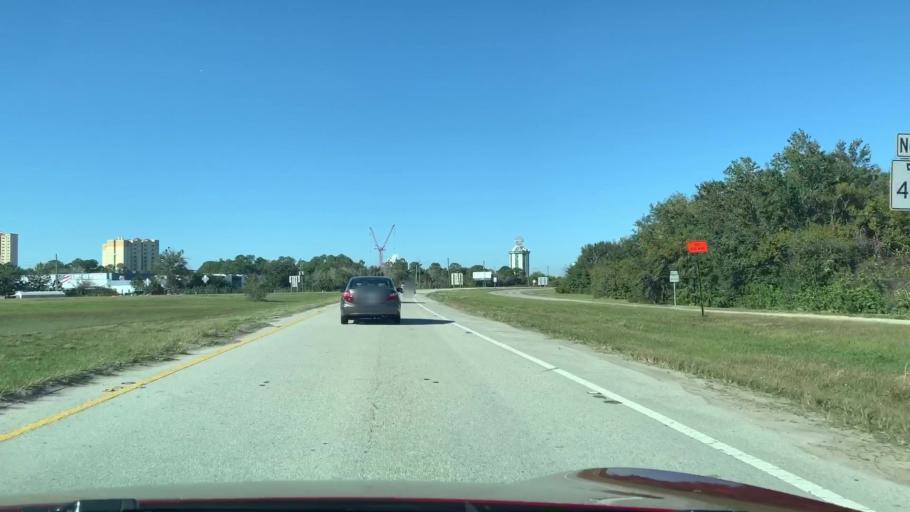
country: US
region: Florida
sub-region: Orange County
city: Tangelo Park
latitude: 28.4520
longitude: -81.4576
